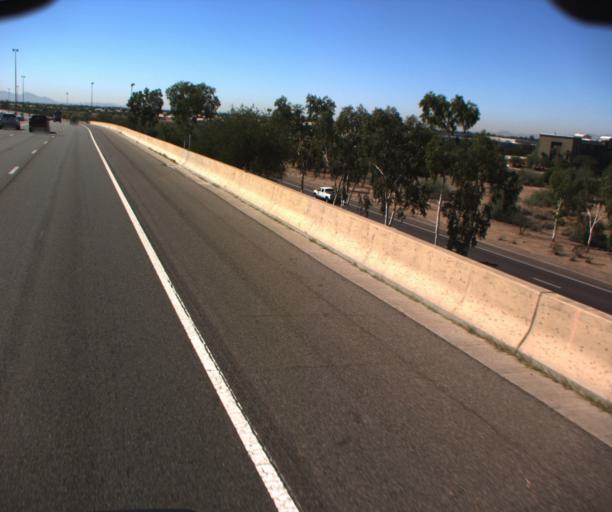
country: US
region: Arizona
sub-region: Maricopa County
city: Sun City
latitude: 33.6373
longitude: -112.2382
